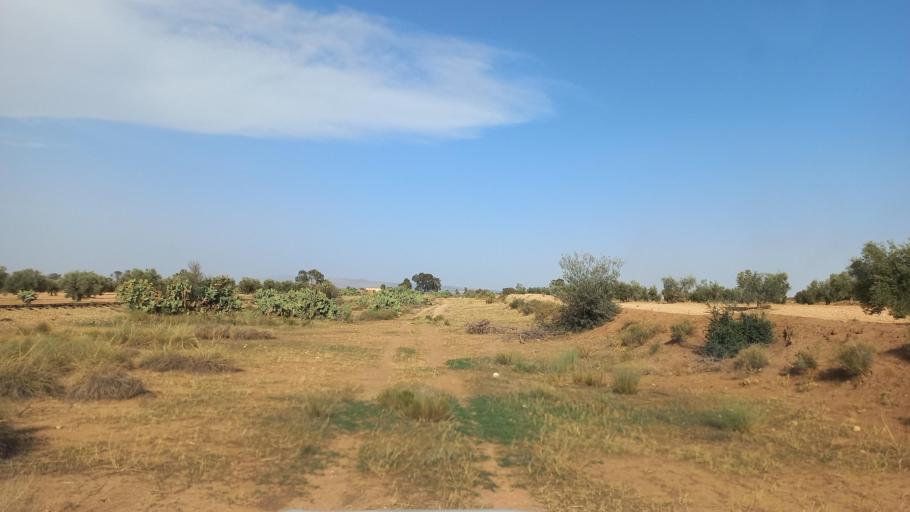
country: TN
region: Al Qasrayn
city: Kasserine
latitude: 35.2235
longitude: 8.9646
